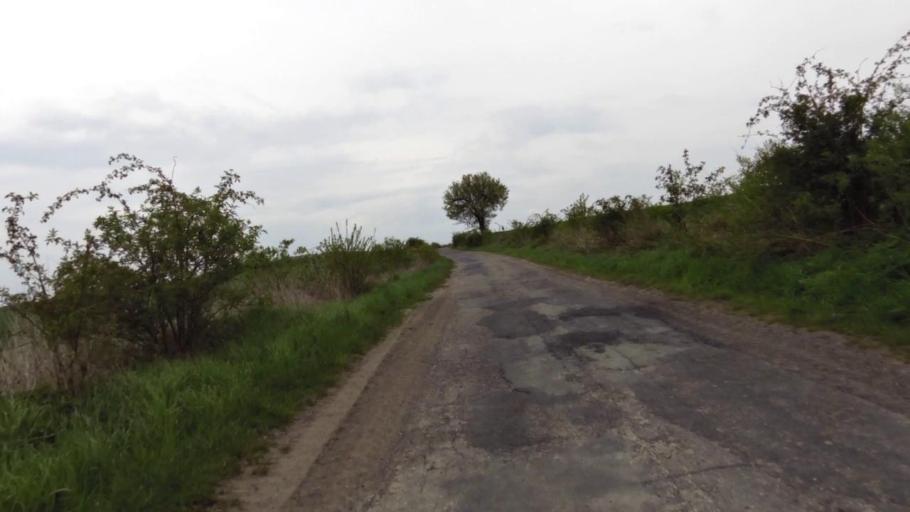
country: PL
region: West Pomeranian Voivodeship
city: Trzcinsko Zdroj
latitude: 52.9542
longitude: 14.6895
